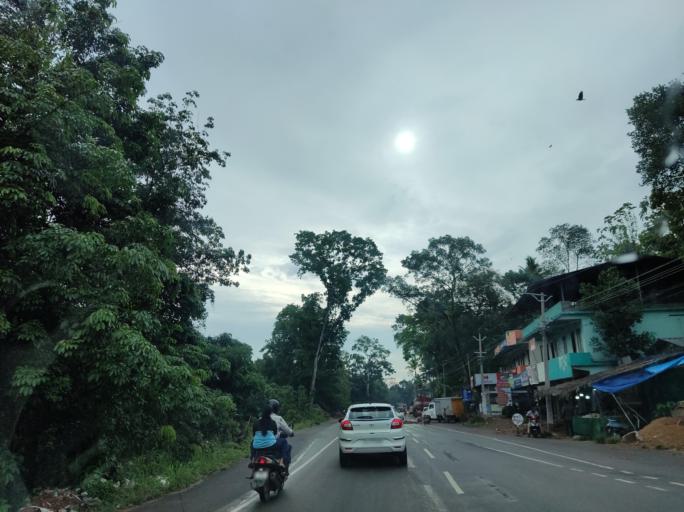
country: IN
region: Kerala
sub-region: Pattanamtitta
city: Adur
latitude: 9.1632
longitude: 76.7037
